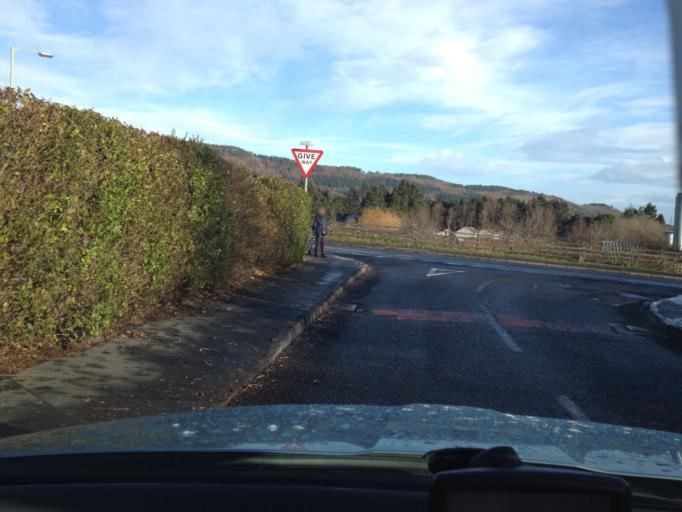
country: GB
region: Scotland
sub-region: Perth and Kinross
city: Bridge of Earn
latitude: 56.3467
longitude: -3.4061
